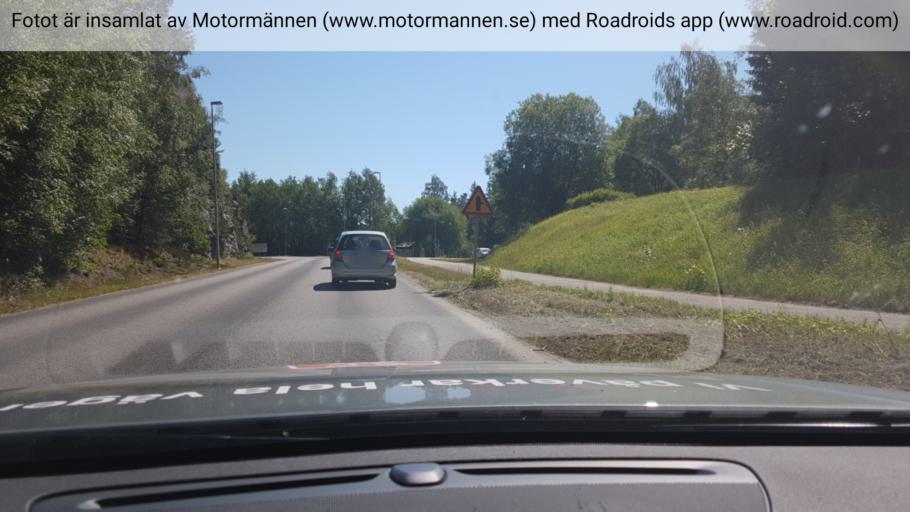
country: SE
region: Stockholm
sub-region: Haninge Kommun
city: Haninge
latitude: 59.1906
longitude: 18.1677
